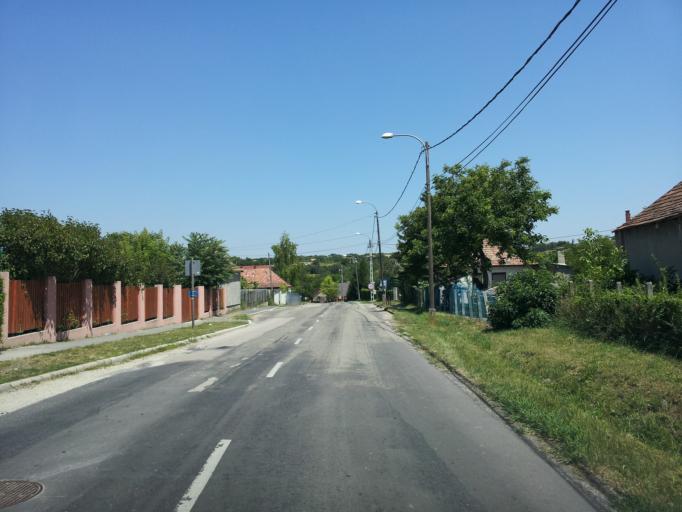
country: HU
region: Veszprem
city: Berhida
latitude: 47.1031
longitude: 18.1432
